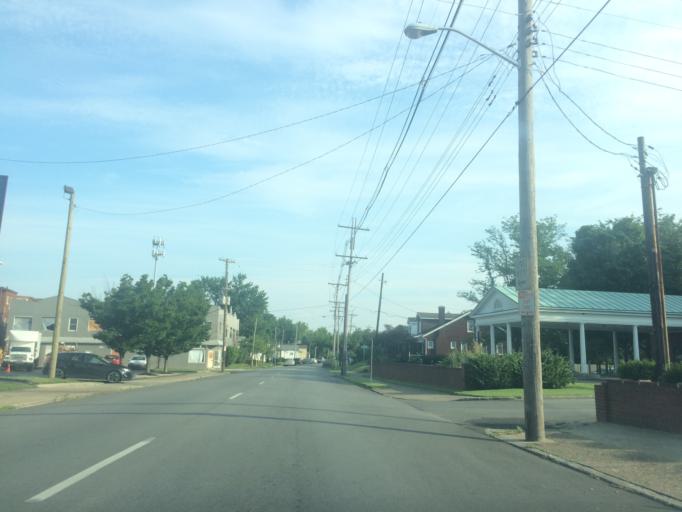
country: US
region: Kentucky
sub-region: Jefferson County
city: Audubon Park
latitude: 38.2152
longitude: -85.7429
